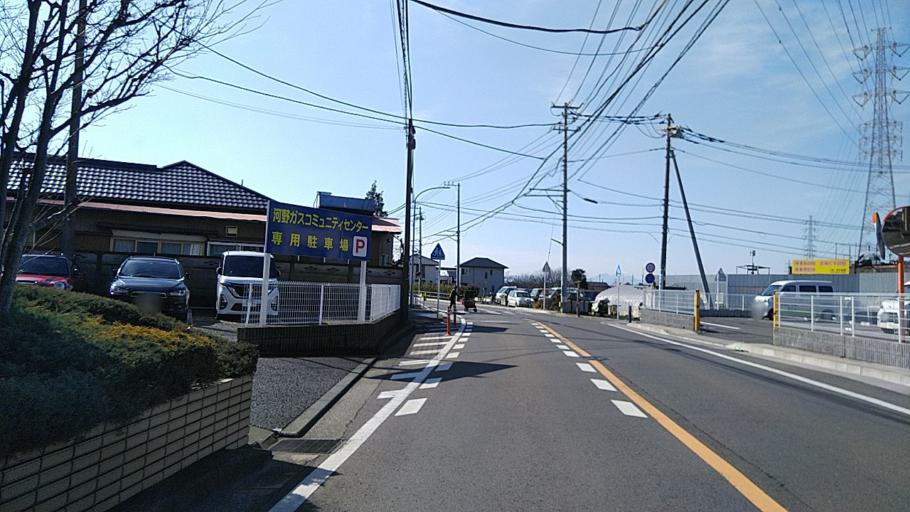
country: JP
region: Kanagawa
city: Fujisawa
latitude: 35.4042
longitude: 139.4958
